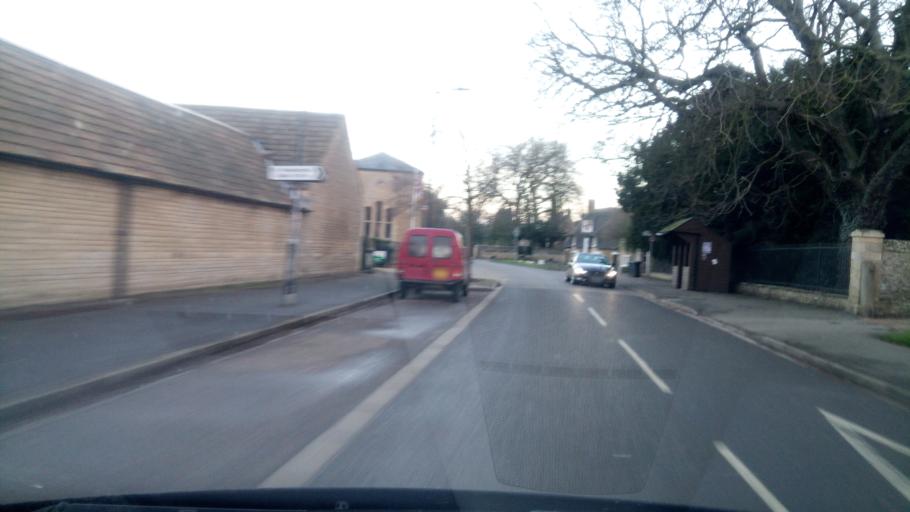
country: GB
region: England
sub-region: Peterborough
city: Castor
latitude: 52.5720
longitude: -0.3440
